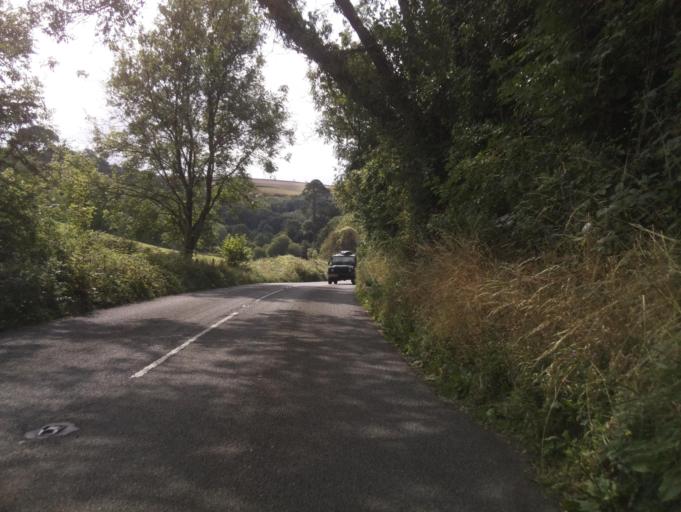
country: GB
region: England
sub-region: Devon
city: Dartmouth
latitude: 50.3616
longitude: -3.5616
